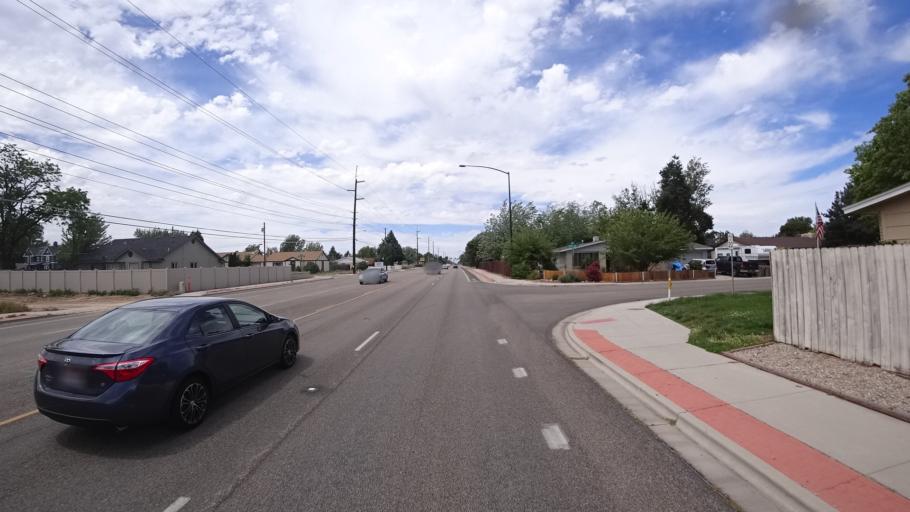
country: US
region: Idaho
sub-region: Ada County
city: Garden City
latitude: 43.6340
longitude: -116.3007
